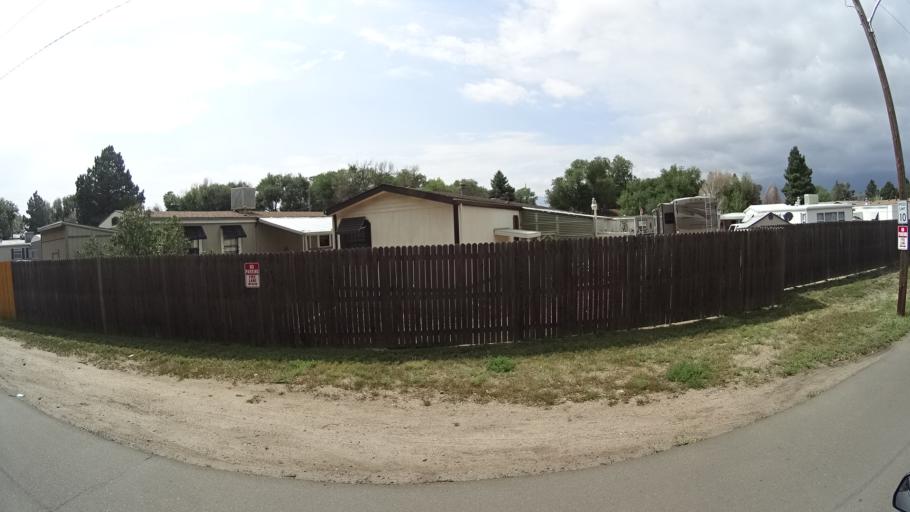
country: US
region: Colorado
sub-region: El Paso County
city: Colorado Springs
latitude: 38.8832
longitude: -104.8241
